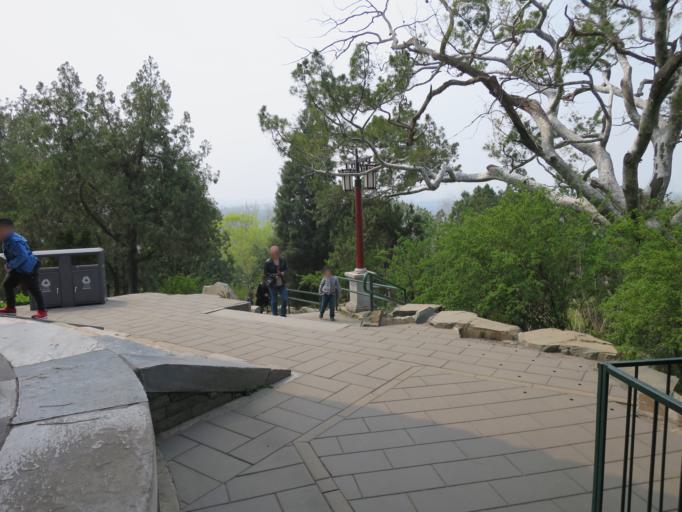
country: CN
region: Beijing
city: Jingshan
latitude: 39.9232
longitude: 116.3886
